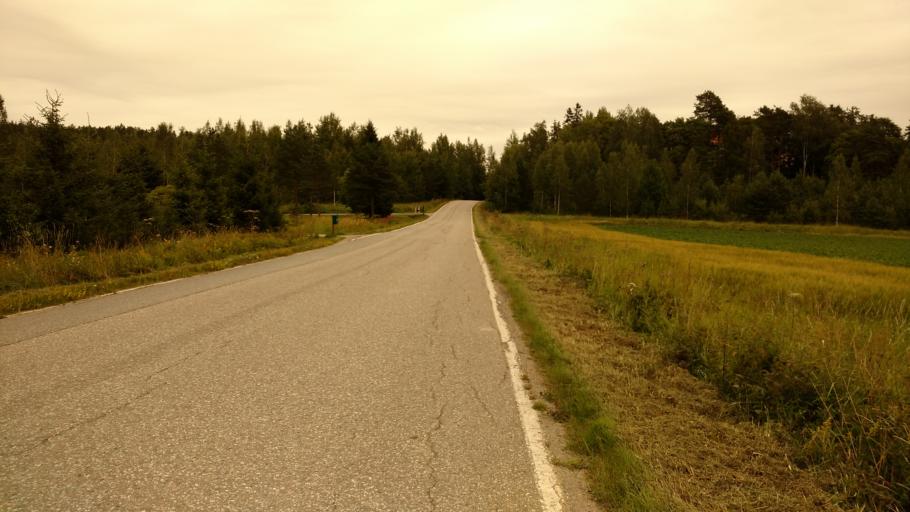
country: FI
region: Varsinais-Suomi
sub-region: Loimaa
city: Marttila
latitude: 60.4152
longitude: 22.8871
